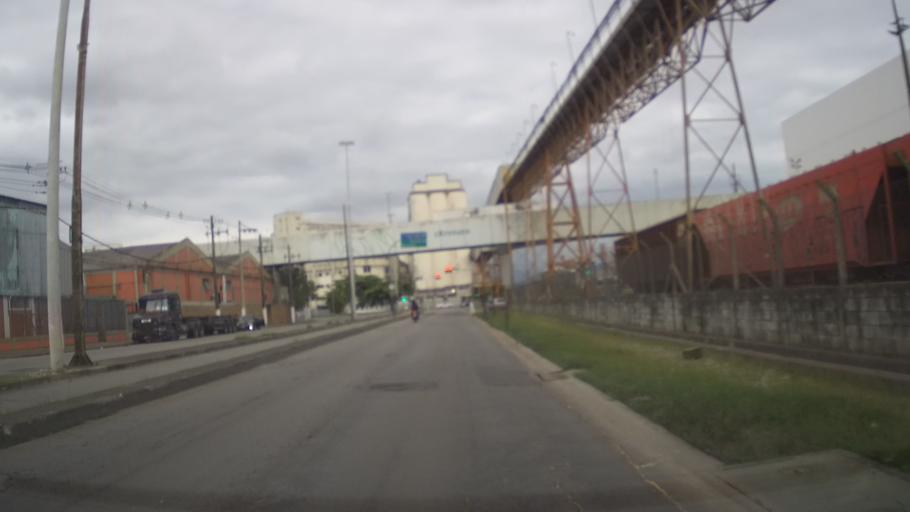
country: BR
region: Sao Paulo
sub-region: Santos
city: Santos
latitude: -23.9621
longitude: -46.3053
